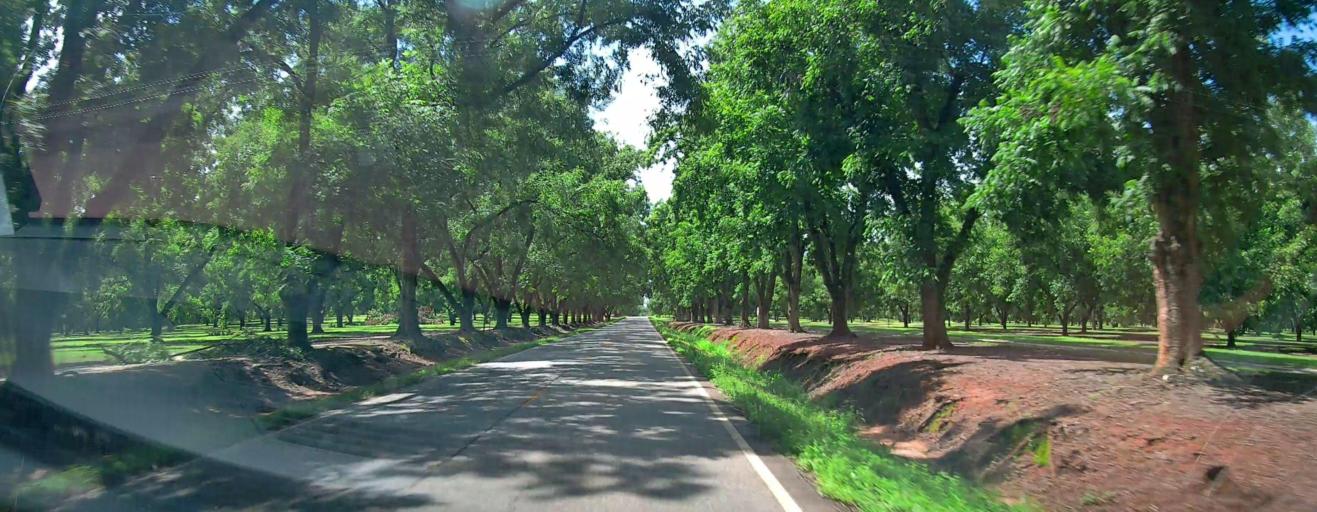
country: US
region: Georgia
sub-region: Houston County
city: Perry
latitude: 32.5212
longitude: -83.7896
